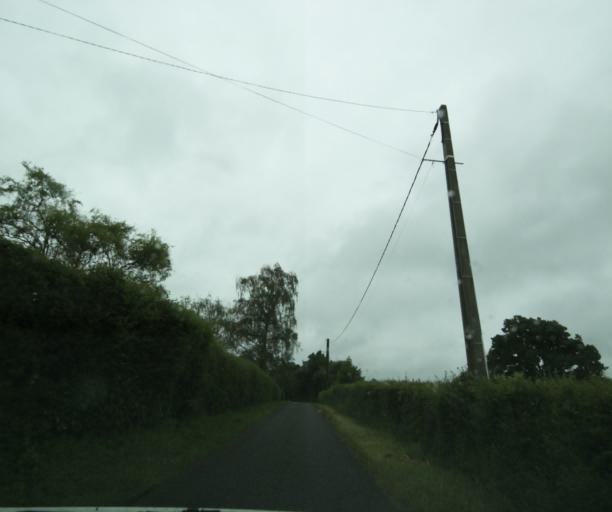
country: FR
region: Bourgogne
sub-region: Departement de Saone-et-Loire
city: Palinges
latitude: 46.5505
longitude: 4.1975
